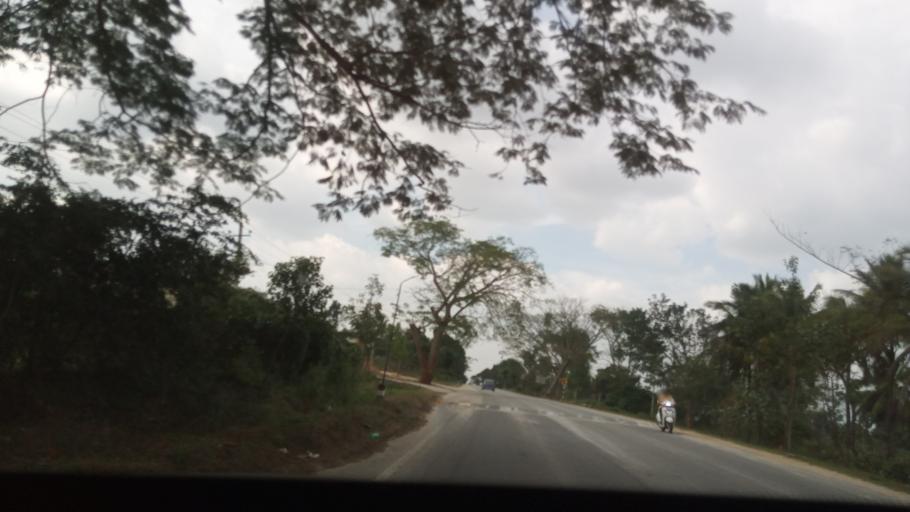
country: IN
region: Karnataka
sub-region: Tumkur
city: Kunigal
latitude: 12.8950
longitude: 77.0440
